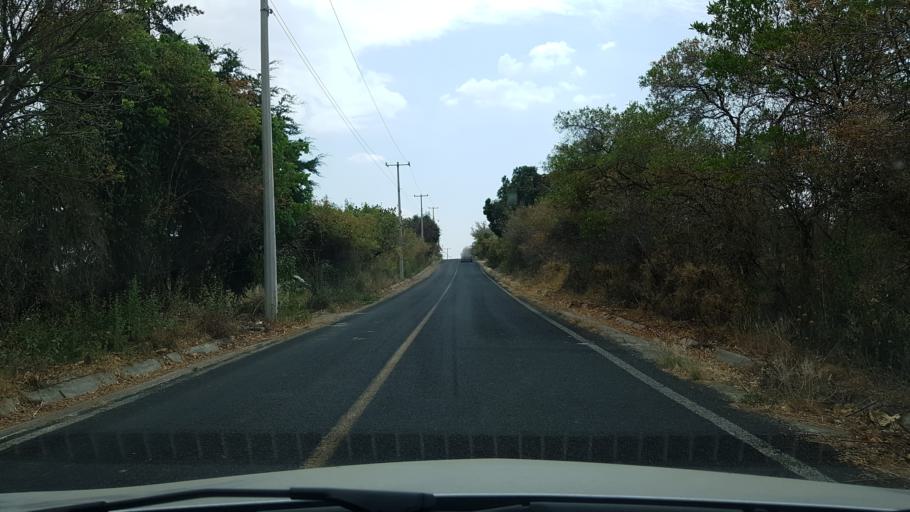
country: MX
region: Puebla
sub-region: Tochimilco
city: San Antonio Alpanocan
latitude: 18.8424
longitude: -98.7167
